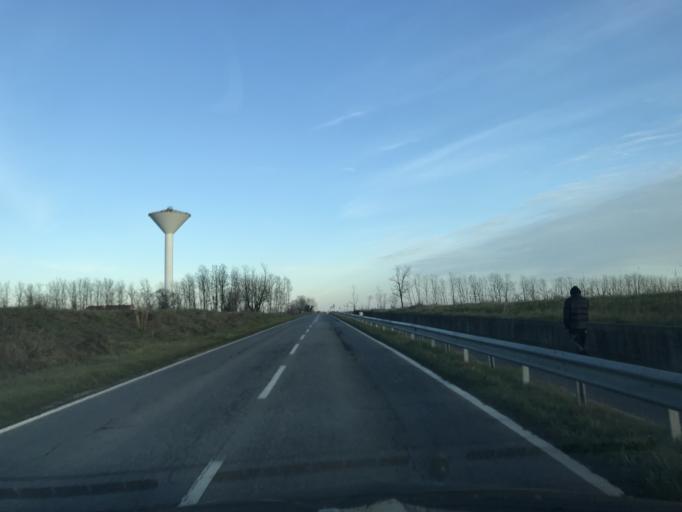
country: IT
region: Lombardy
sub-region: Provincia di Lodi
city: Graffignana
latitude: 45.2123
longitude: 9.4732
